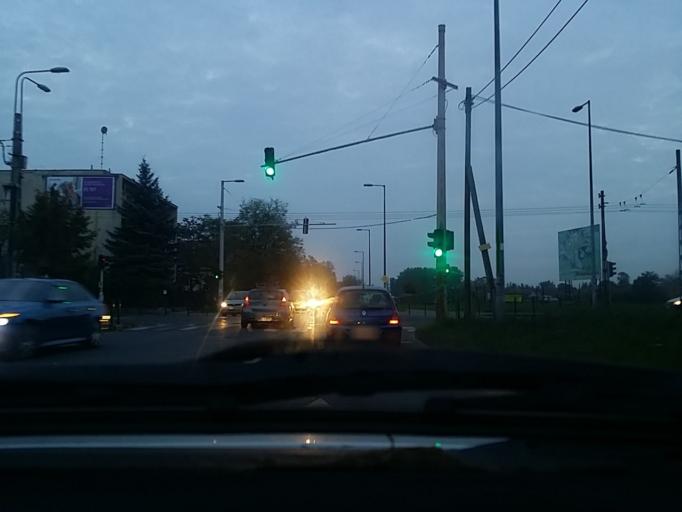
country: HU
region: Budapest
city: Budapest XIV. keruelet
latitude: 47.5253
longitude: 19.1247
